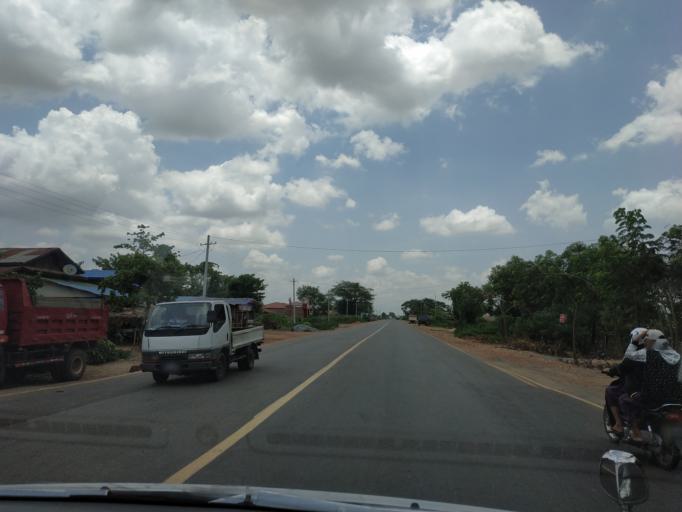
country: MM
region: Bago
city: Bago
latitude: 17.4713
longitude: 96.5485
